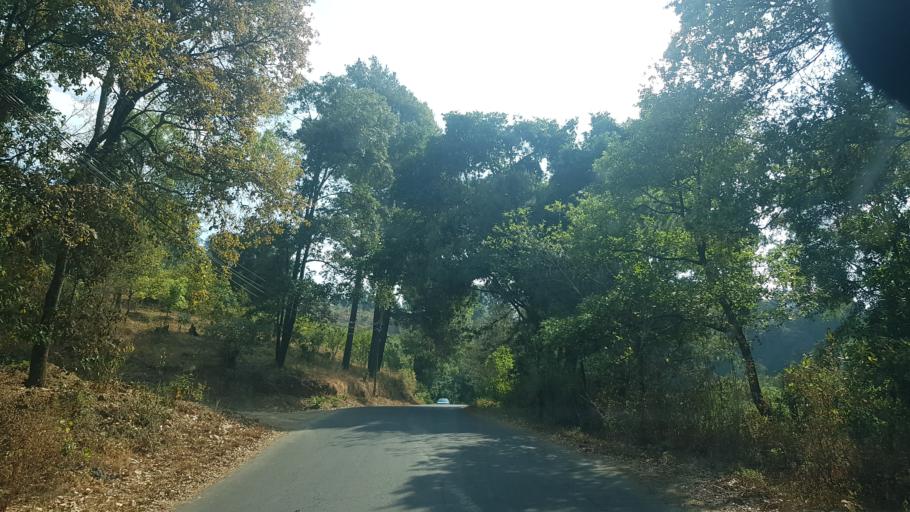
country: MX
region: Puebla
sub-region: Tochimilco
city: San Antonio Alpanocan
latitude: 18.8775
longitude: -98.6986
